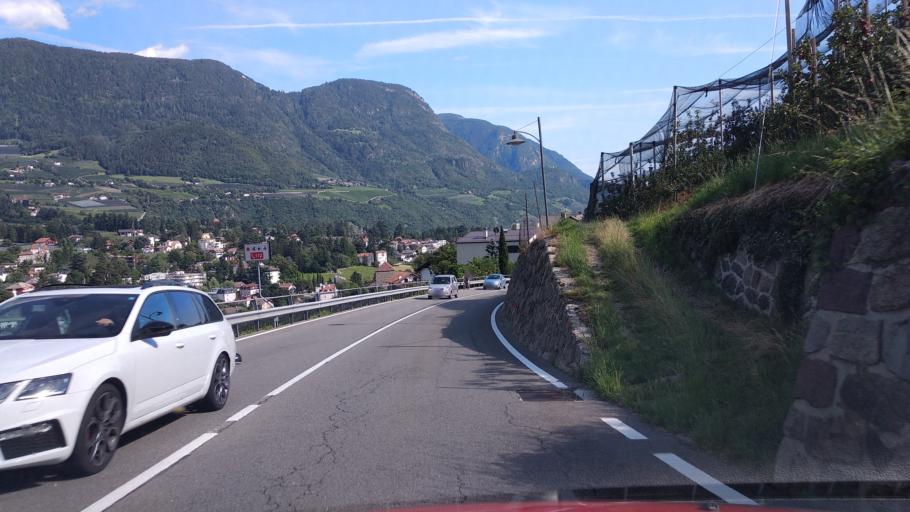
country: IT
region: Trentino-Alto Adige
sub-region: Bolzano
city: Merano
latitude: 46.6768
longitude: 11.1691
